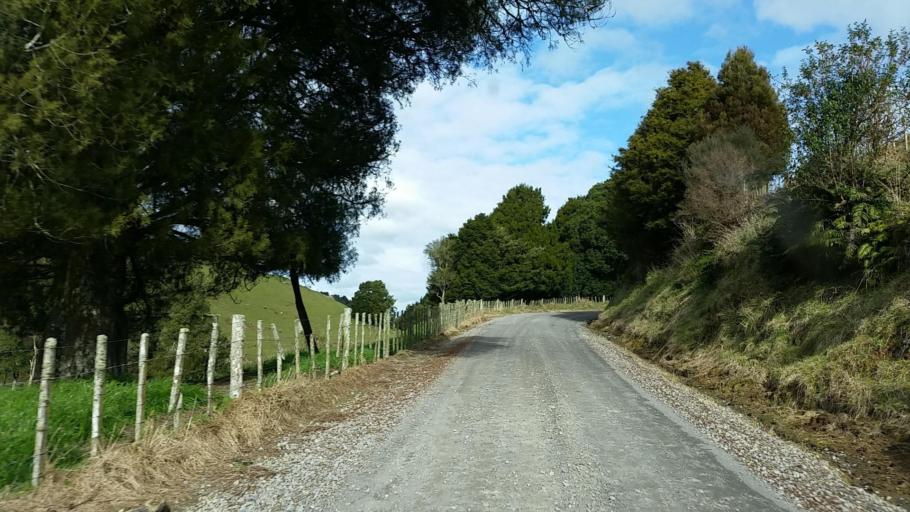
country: NZ
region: Taranaki
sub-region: New Plymouth District
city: Waitara
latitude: -39.1507
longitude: 174.5597
